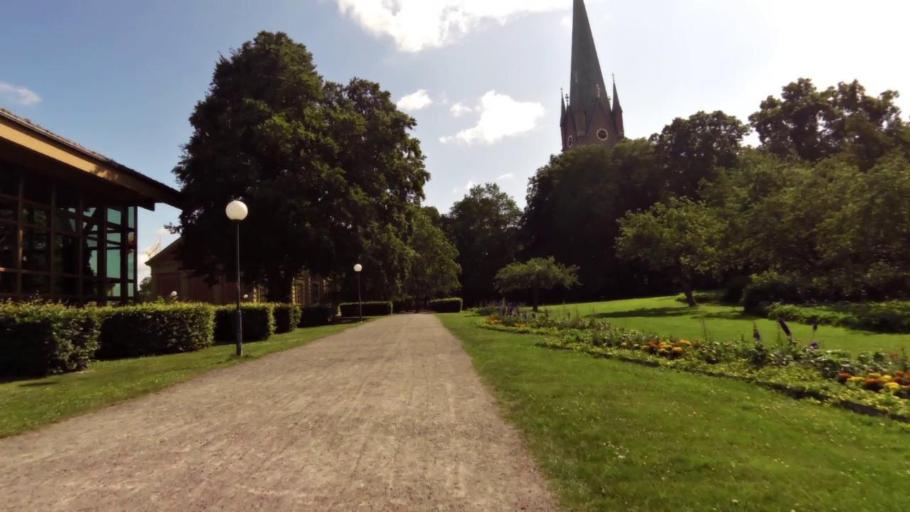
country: SE
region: OEstergoetland
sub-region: Linkopings Kommun
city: Linkoping
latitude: 58.4113
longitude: 15.6140
